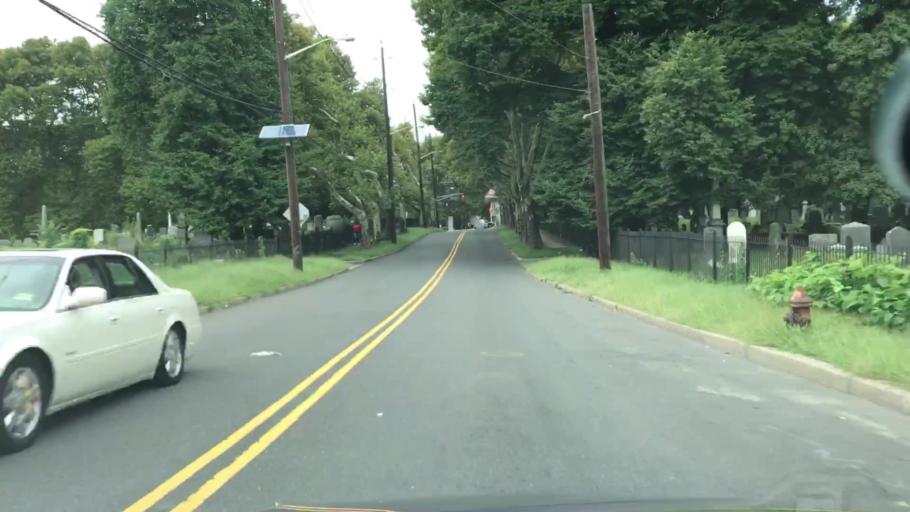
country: US
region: New Jersey
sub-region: Hudson County
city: Jersey City
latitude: 40.6953
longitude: -74.0841
